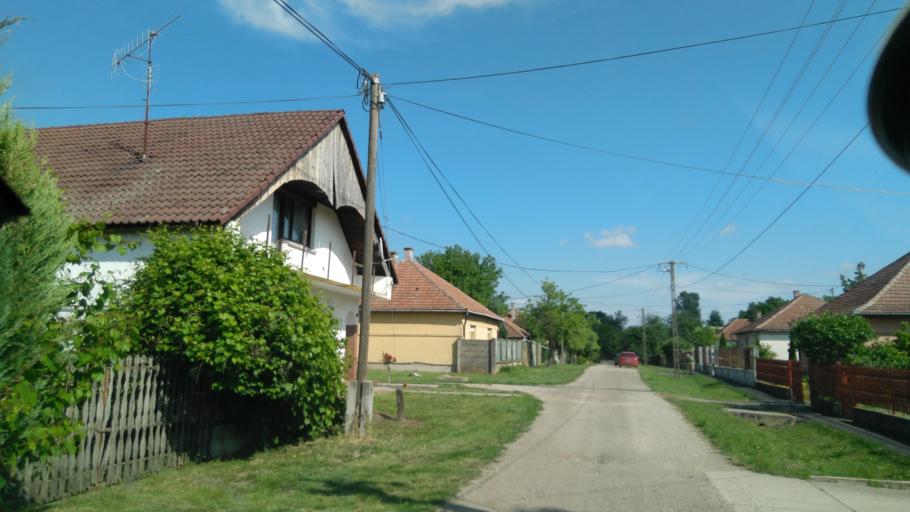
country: HU
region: Bekes
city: Doboz
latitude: 46.7010
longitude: 21.1903
